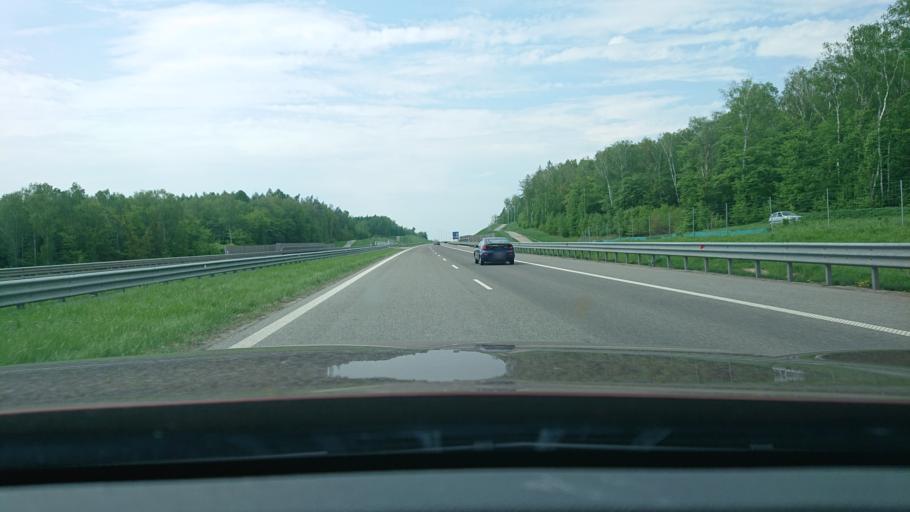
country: PL
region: Subcarpathian Voivodeship
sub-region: Powiat jaroslawski
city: Pawlosiow
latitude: 49.9919
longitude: 22.6097
